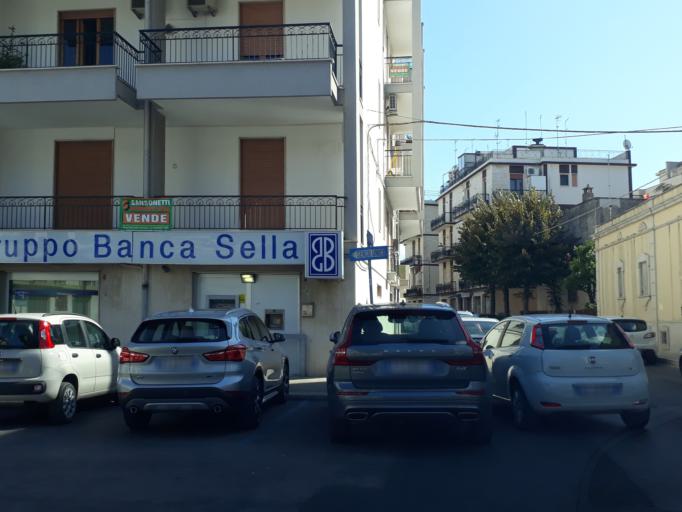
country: IT
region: Apulia
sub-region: Provincia di Brindisi
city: Fasano
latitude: 40.8319
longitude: 17.3582
